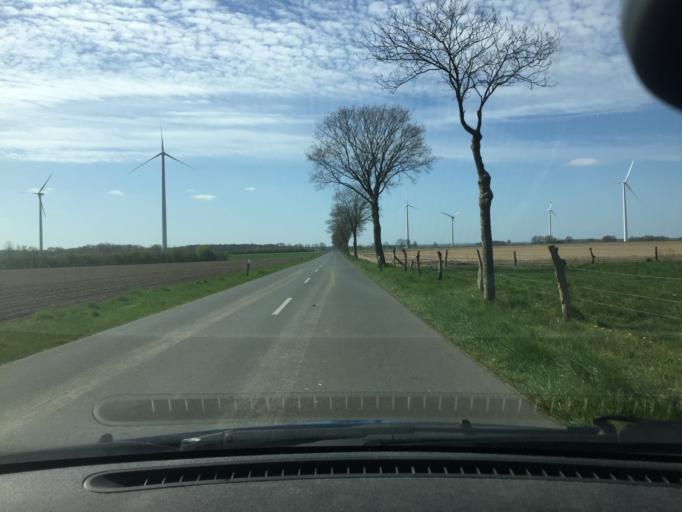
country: DE
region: Lower Saxony
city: Ratzlingen
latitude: 52.9521
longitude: 10.6667
